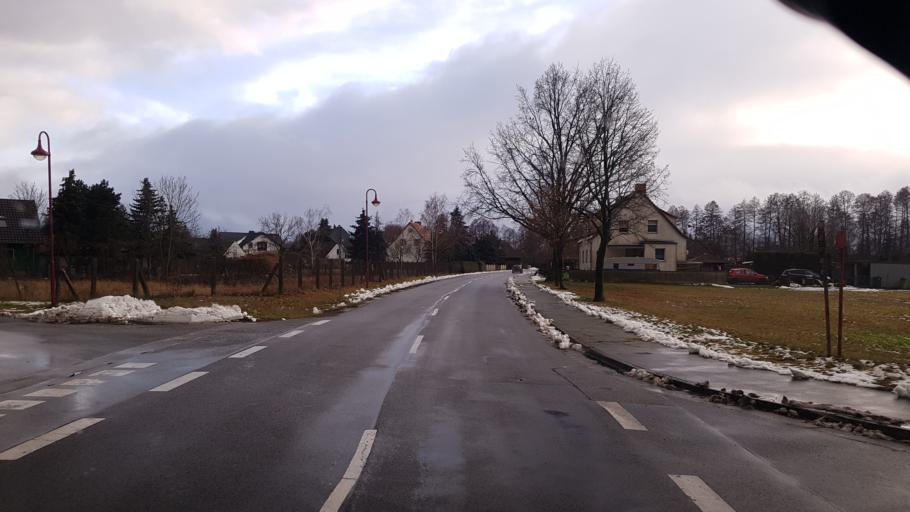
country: DE
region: Brandenburg
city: Heinersbruck
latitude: 51.8230
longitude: 14.5082
